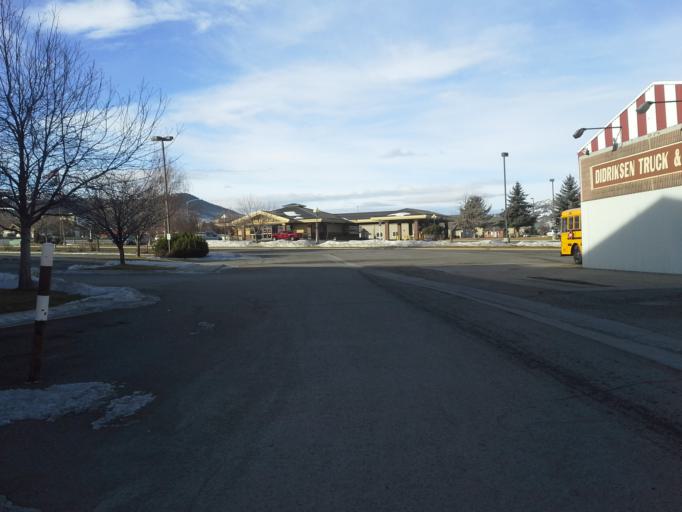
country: US
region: Montana
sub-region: Lewis and Clark County
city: Helena
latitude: 46.5921
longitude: -111.9856
